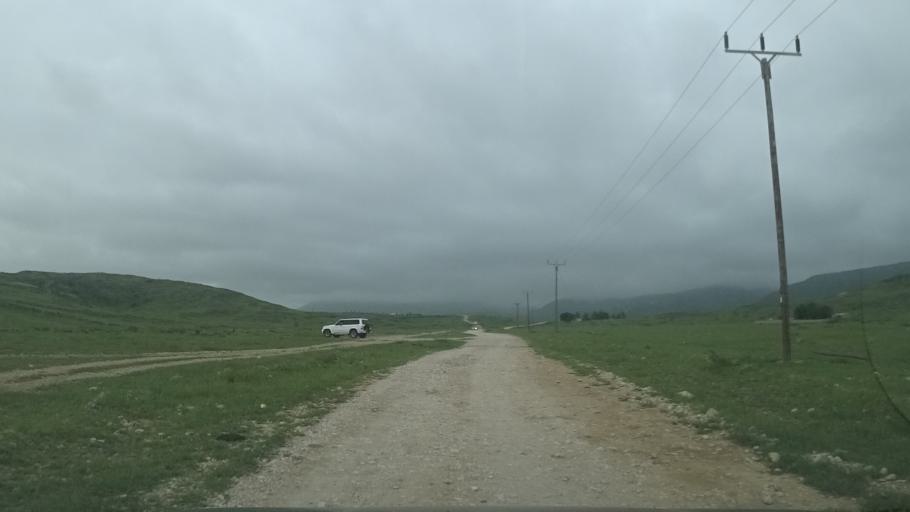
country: OM
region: Zufar
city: Salalah
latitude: 17.1141
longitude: 54.2336
